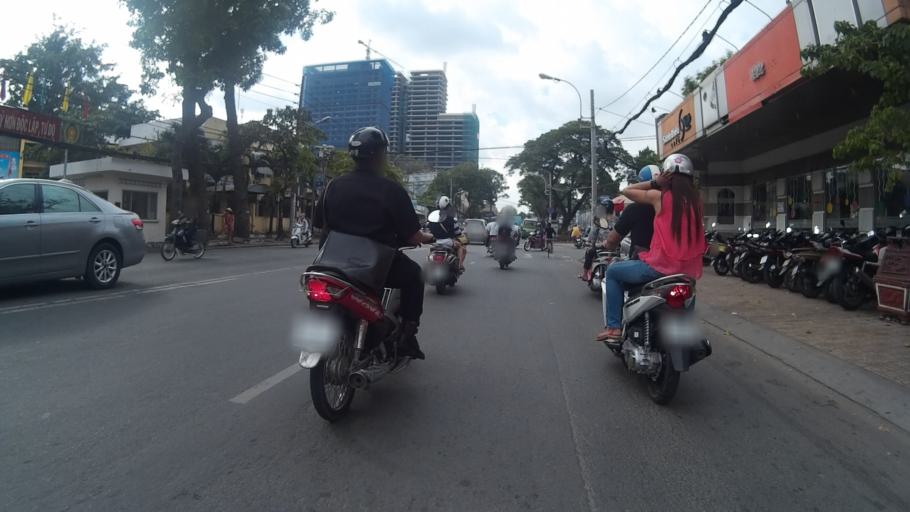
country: VN
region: Ho Chi Minh City
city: Quan Ba
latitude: 10.7771
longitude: 106.6831
